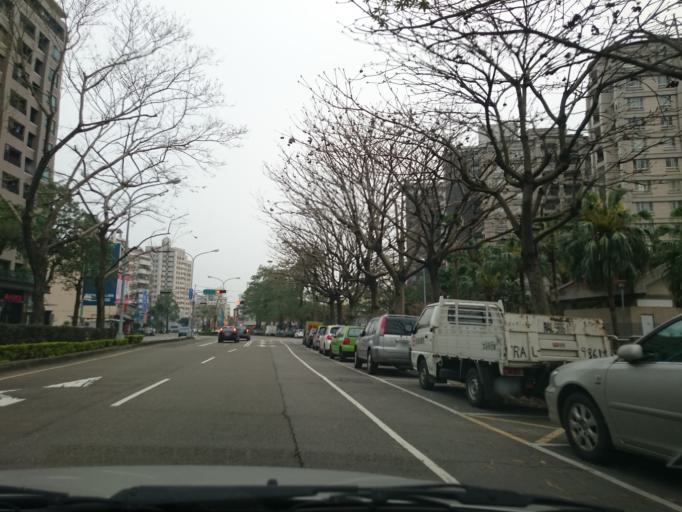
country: TW
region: Taiwan
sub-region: Taichung City
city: Taichung
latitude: 24.1433
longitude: 120.6406
